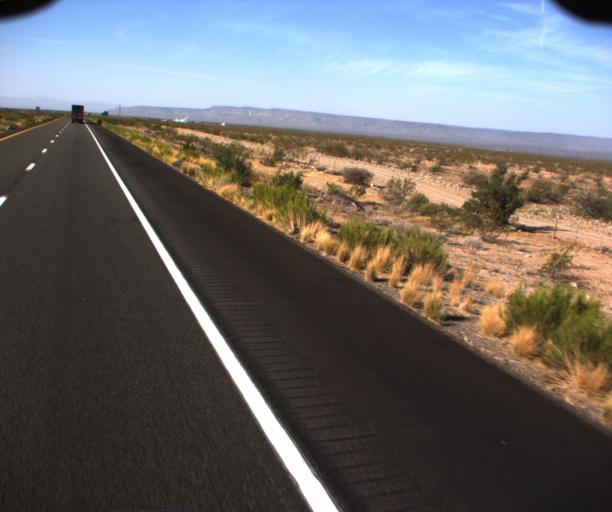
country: US
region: Arizona
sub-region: Mohave County
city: Kingman
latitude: 35.0473
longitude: -114.1283
